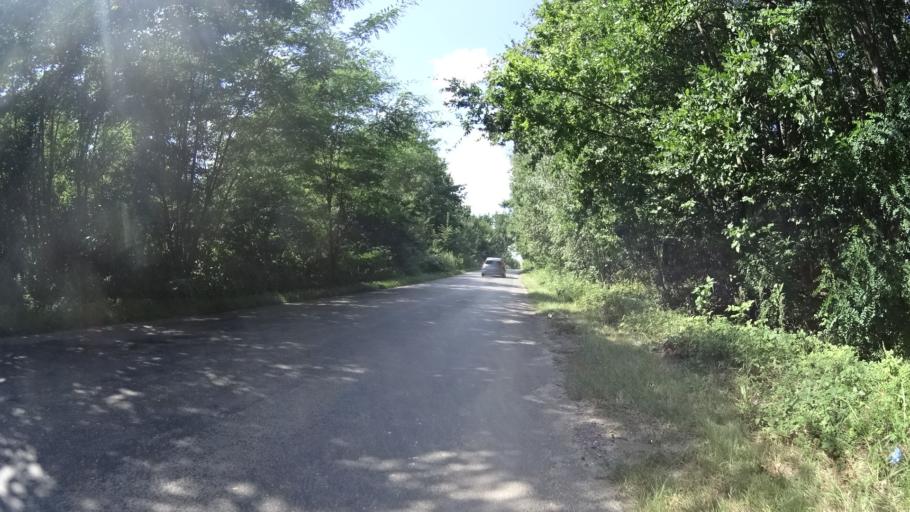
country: PL
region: Masovian Voivodeship
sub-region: Powiat grojecki
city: Mogielnica
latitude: 51.6920
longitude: 20.7381
